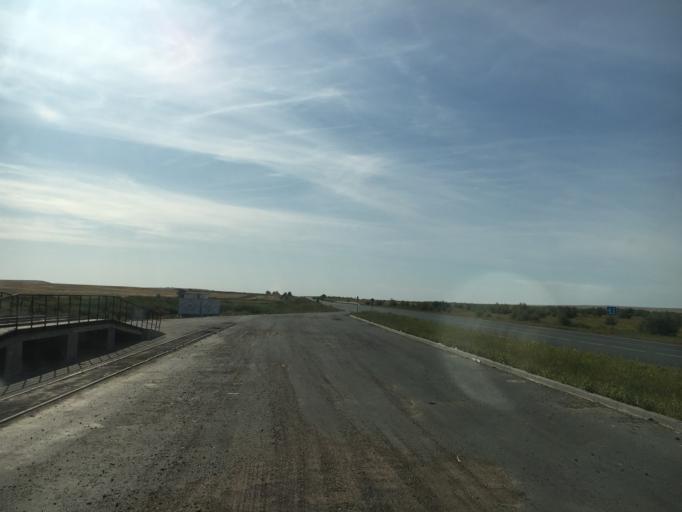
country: KZ
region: Batys Qazaqstan
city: Kamenka
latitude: 51.1071
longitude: 50.4135
